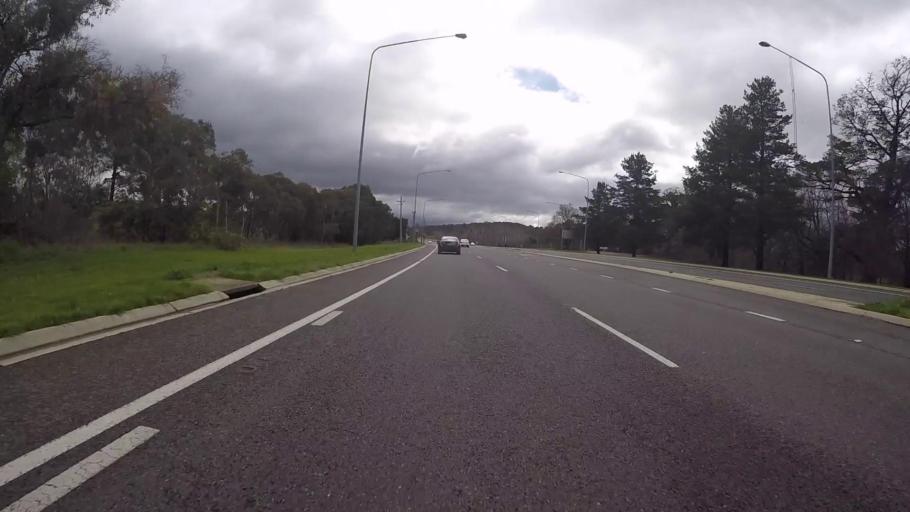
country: AU
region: Australian Capital Territory
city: Kaleen
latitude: -35.2205
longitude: 149.1196
